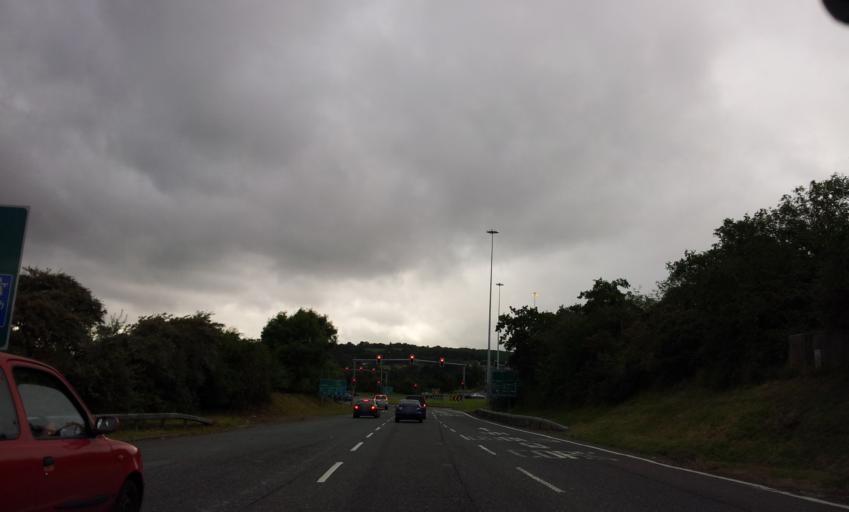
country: IE
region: Munster
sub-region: County Cork
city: Passage West
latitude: 51.9033
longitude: -8.3855
